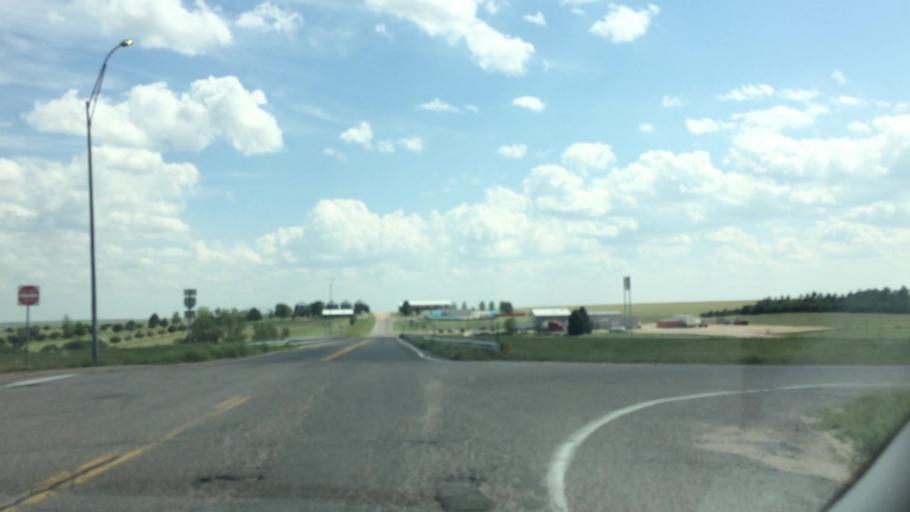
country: US
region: Colorado
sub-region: Lincoln County
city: Hugo
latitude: 39.2869
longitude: -103.0619
